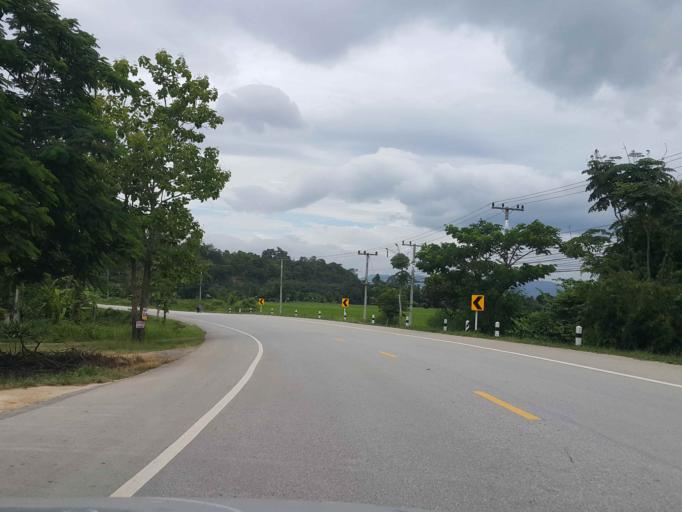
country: TH
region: Lamphun
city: Li
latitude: 17.7621
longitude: 98.9983
